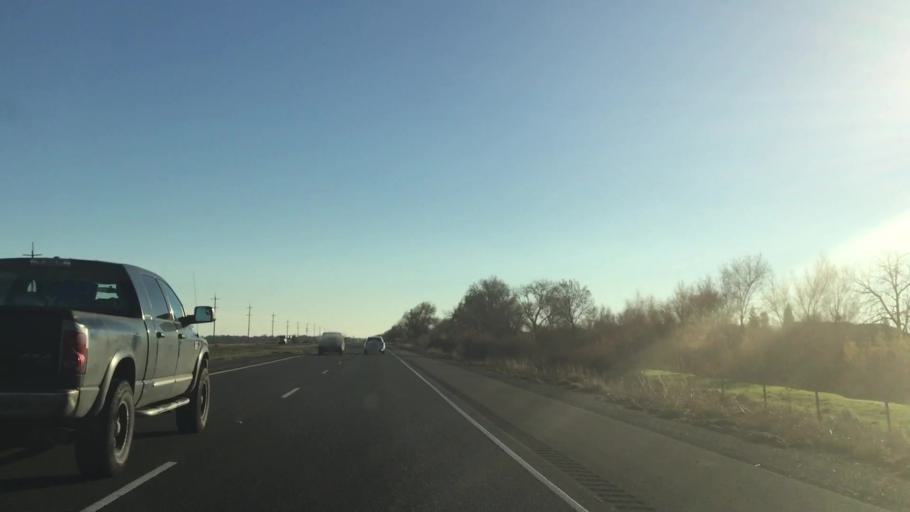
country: US
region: California
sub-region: Yuba County
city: Plumas Lake
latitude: 39.0058
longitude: -121.5435
